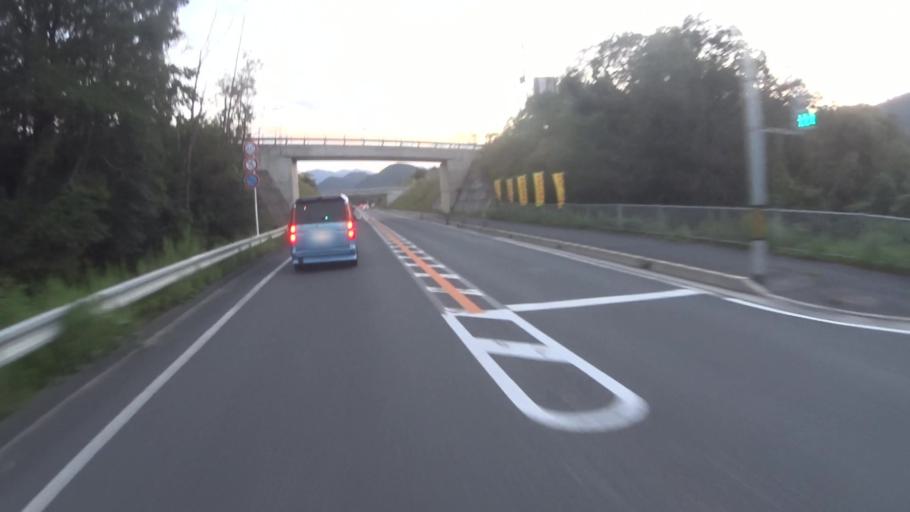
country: JP
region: Kyoto
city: Ayabe
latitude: 35.2036
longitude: 135.4311
